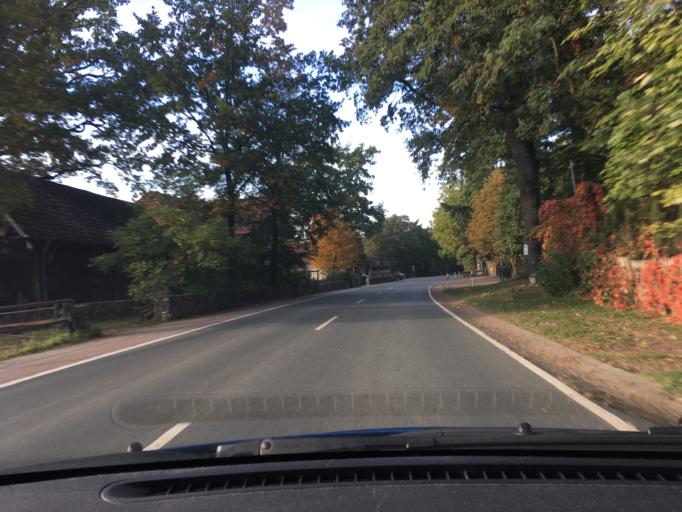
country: DE
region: Lower Saxony
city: Fassberg
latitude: 52.9175
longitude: 10.1277
